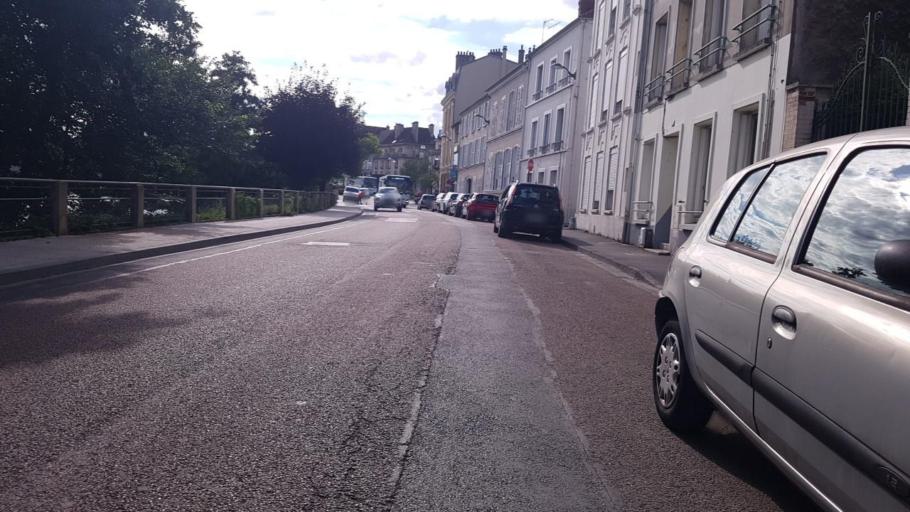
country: FR
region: Picardie
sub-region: Departement de l'Aisne
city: Chateau-Thierry
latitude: 49.0443
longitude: 3.4054
